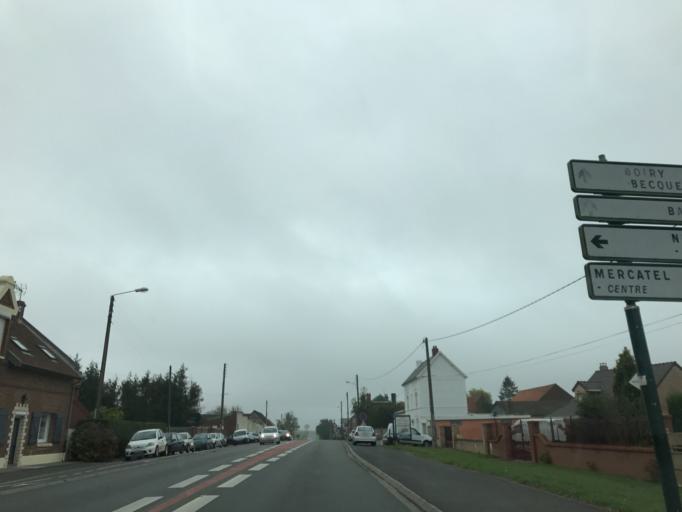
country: FR
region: Nord-Pas-de-Calais
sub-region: Departement du Pas-de-Calais
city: Beaurains
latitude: 50.2380
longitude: 2.7997
